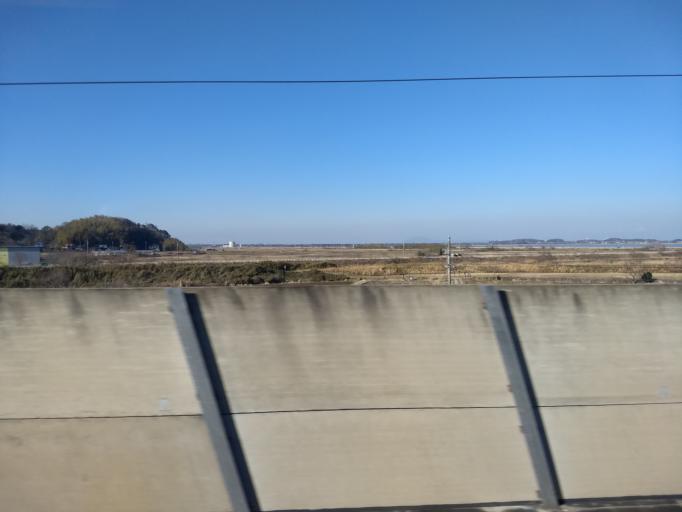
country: JP
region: Chiba
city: Narita
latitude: 35.7871
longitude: 140.2461
